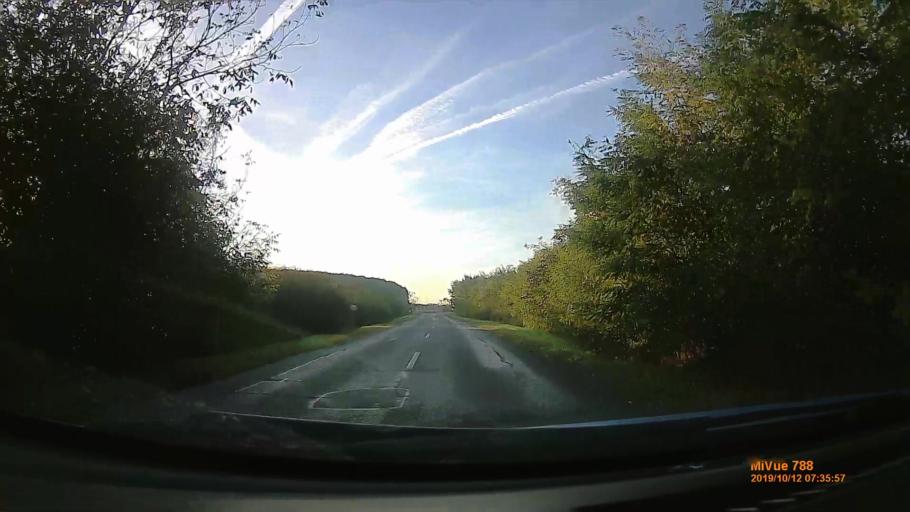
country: HU
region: Hajdu-Bihar
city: Pocsaj
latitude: 47.2494
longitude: 21.8117
